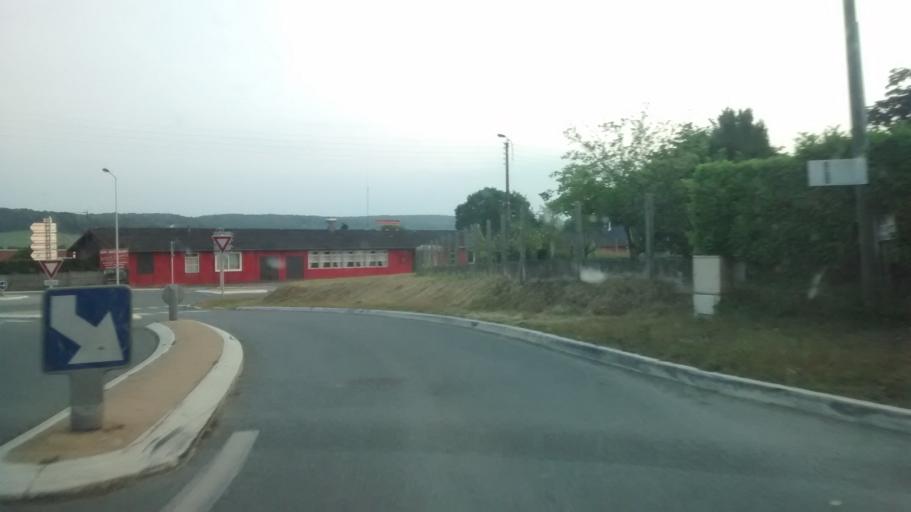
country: FR
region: Brittany
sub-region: Departement du Morbihan
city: Guer
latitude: 47.9100
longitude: -2.1339
